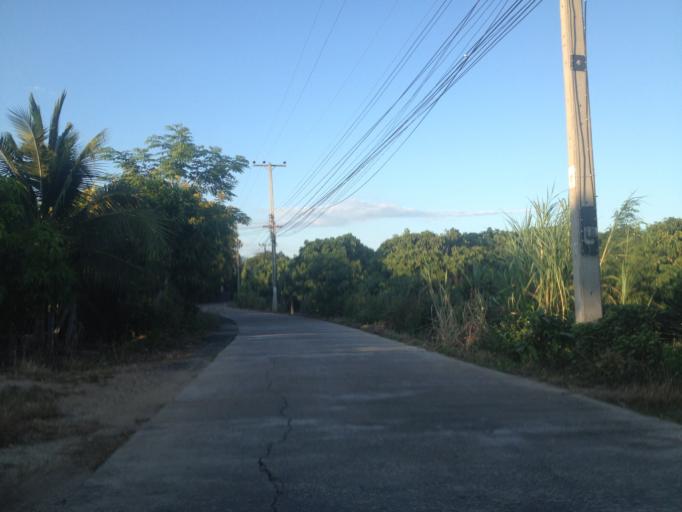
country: TH
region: Chiang Mai
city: San Pa Tong
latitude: 18.6544
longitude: 98.8872
